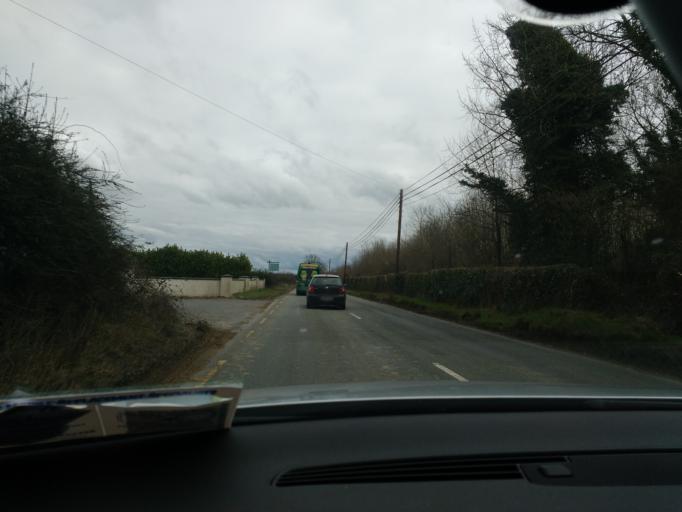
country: IE
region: Leinster
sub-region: Kilkenny
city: Ballyragget
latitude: 52.7327
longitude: -7.4428
